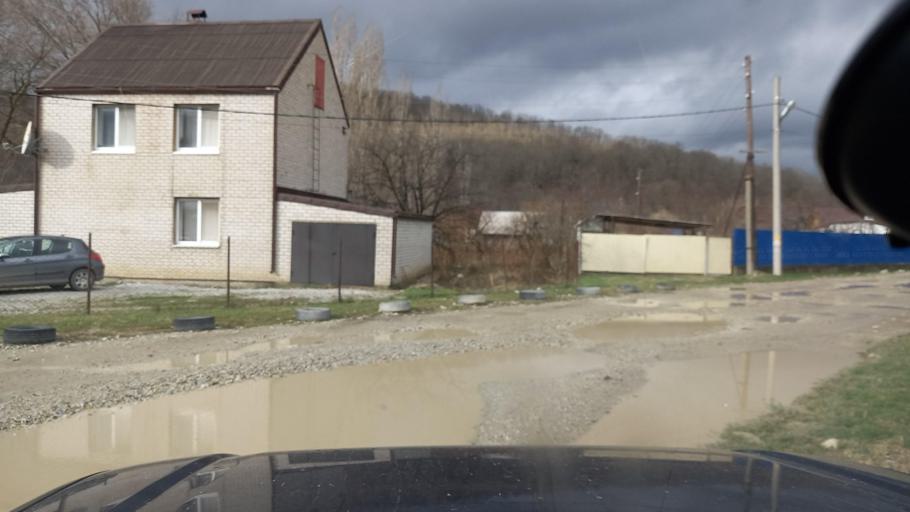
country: RU
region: Krasnodarskiy
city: Pshada
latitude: 44.4794
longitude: 38.4021
